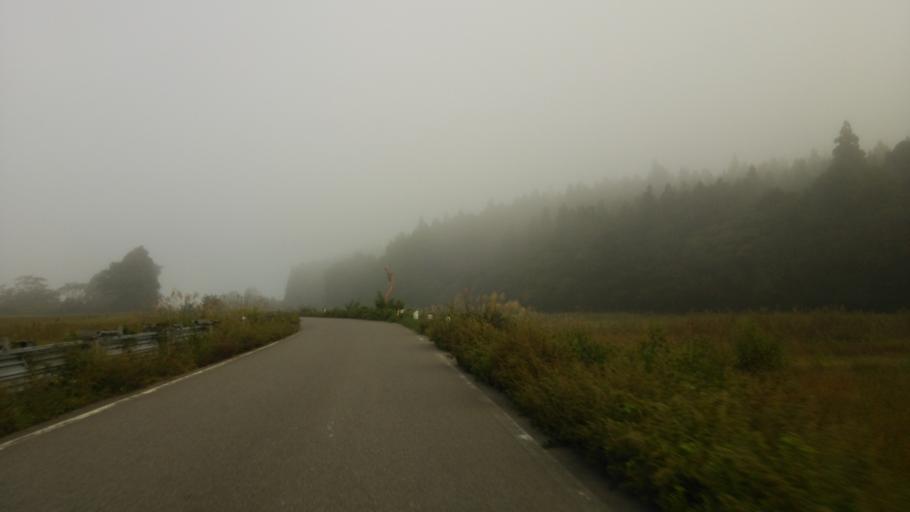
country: JP
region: Fukushima
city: Kitakata
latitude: 37.5844
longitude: 139.7752
